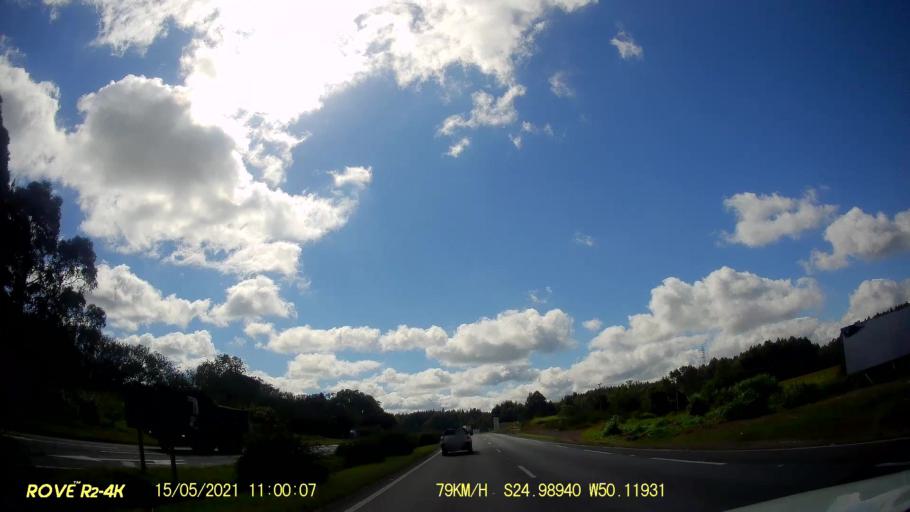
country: BR
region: Parana
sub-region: Carambei
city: Carambei
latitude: -24.9894
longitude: -50.1194
